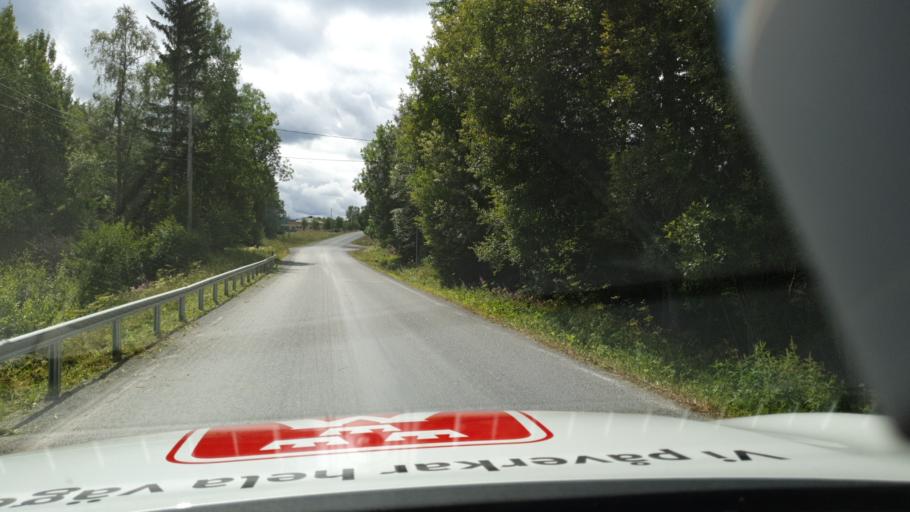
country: SE
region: Jaemtland
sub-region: Bergs Kommun
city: Hoverberg
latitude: 62.9075
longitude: 14.3137
